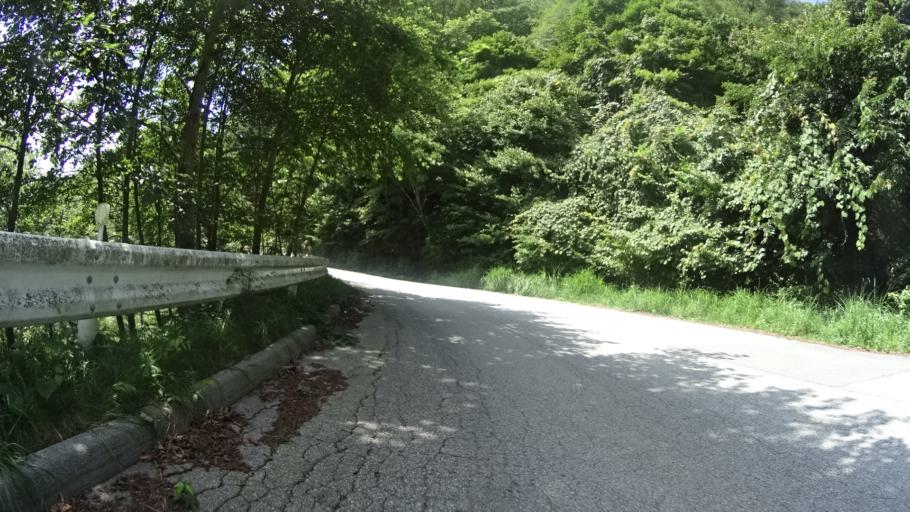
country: JP
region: Yamanashi
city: Enzan
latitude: 35.8040
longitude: 138.6701
